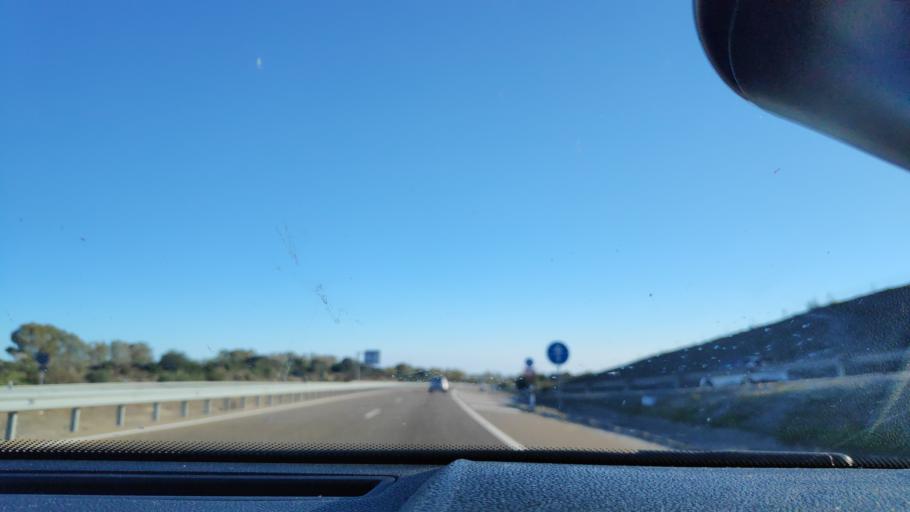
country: ES
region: Andalusia
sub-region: Provincia de Sevilla
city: Guillena
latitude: 37.5722
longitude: -6.1066
